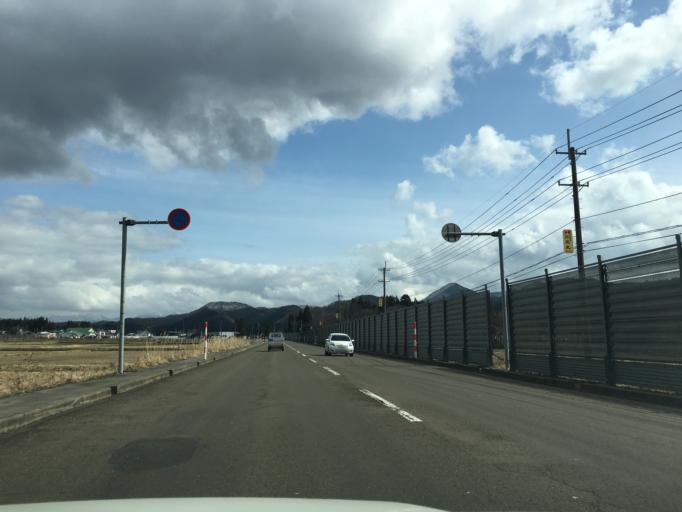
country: JP
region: Akita
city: Odate
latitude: 40.2164
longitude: 140.6187
